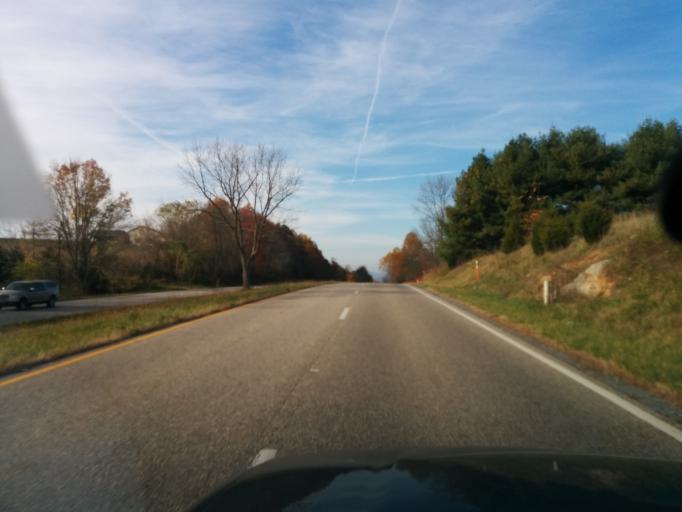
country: US
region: Virginia
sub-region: Rockbridge County
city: East Lexington
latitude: 37.8580
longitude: -79.3235
